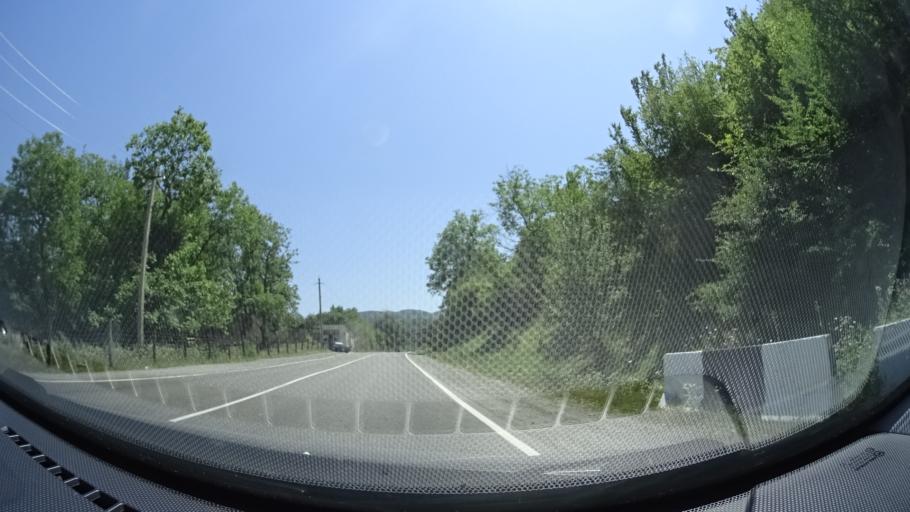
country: GE
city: Zhinvali
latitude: 42.1685
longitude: 44.6962
